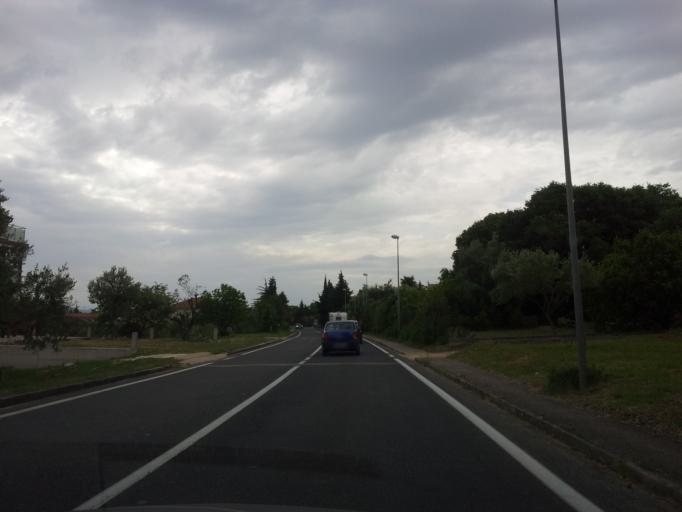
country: HR
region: Zadarska
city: Sveti Filip i Jakov
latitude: 43.9614
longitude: 15.4317
